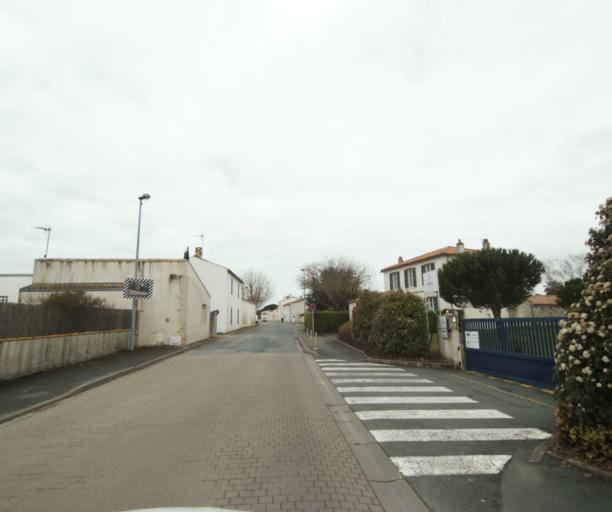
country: FR
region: Poitou-Charentes
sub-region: Departement de la Charente-Maritime
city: Lagord
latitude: 46.1910
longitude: -1.1491
